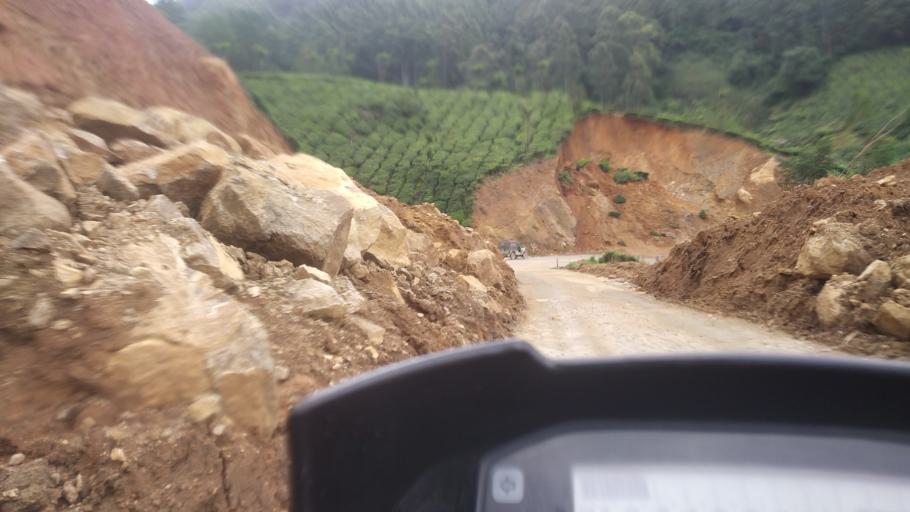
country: IN
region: Kerala
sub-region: Idukki
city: Munnar
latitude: 10.0368
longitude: 77.1519
